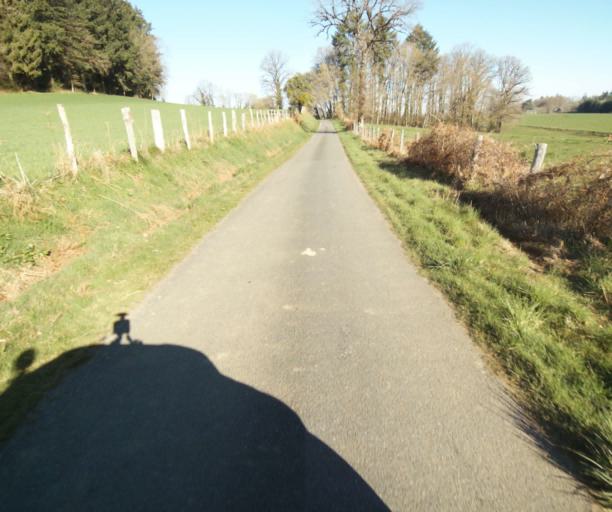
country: FR
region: Limousin
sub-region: Departement de la Correze
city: Chamboulive
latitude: 45.4095
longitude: 1.6933
